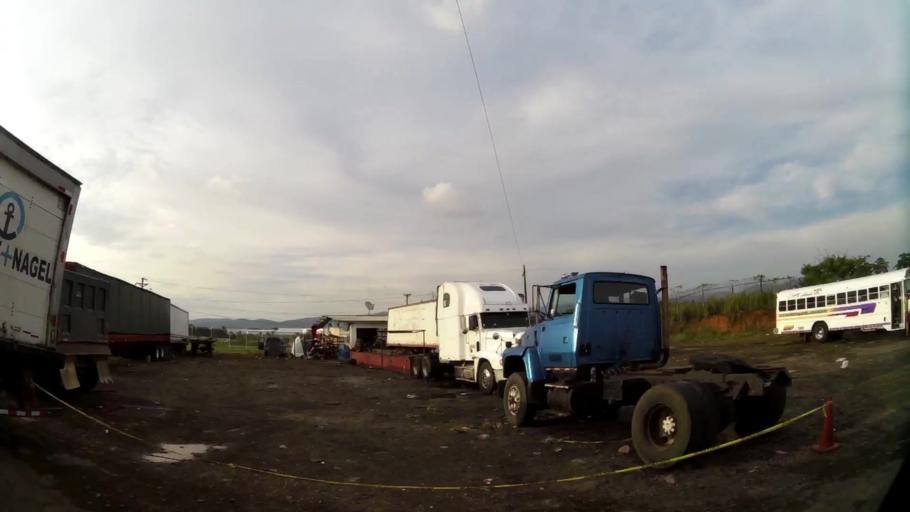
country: PA
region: Panama
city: Tocumen
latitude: 9.0783
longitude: -79.3699
